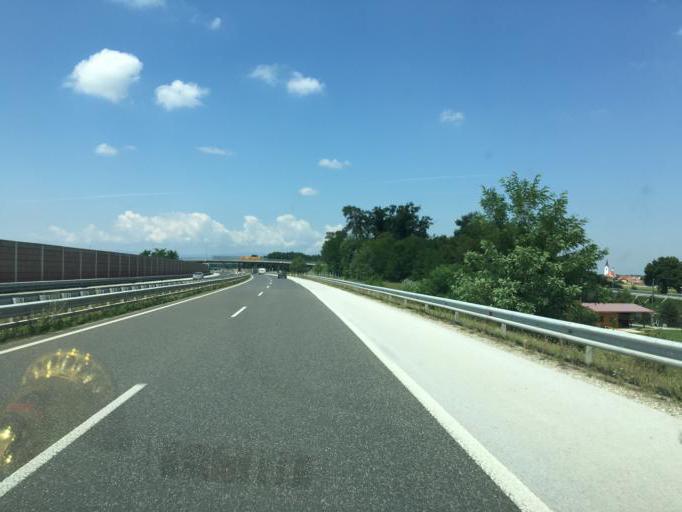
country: SI
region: Hajdina
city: Spodnja Hajdina
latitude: 46.3973
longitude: 15.8469
